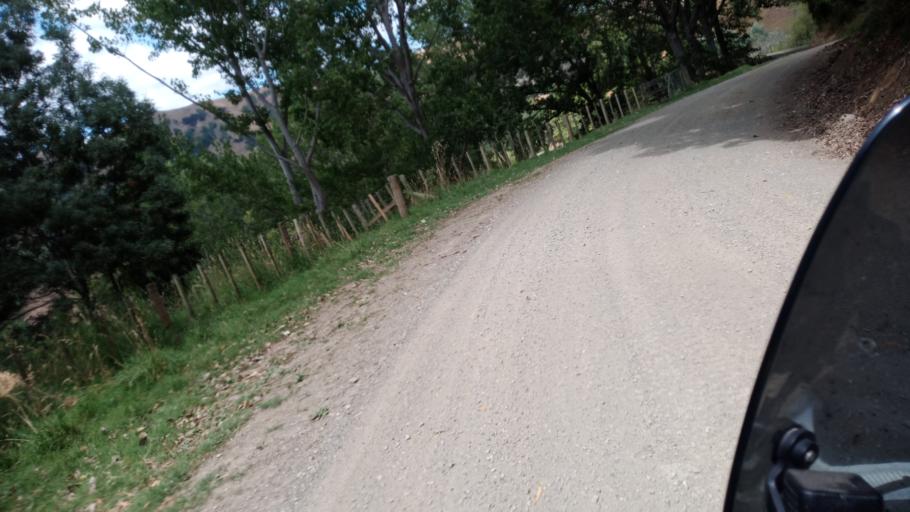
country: NZ
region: Gisborne
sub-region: Gisborne District
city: Gisborne
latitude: -38.4824
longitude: 177.6898
